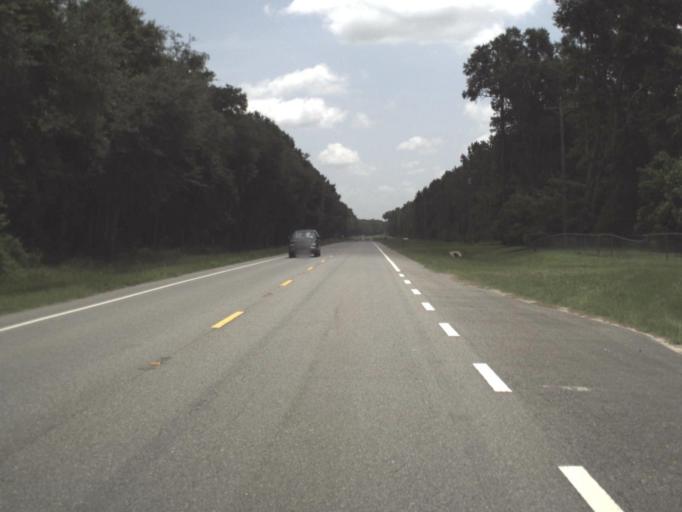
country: US
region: Florida
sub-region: Madison County
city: Madison
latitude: 30.4854
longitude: -83.5249
